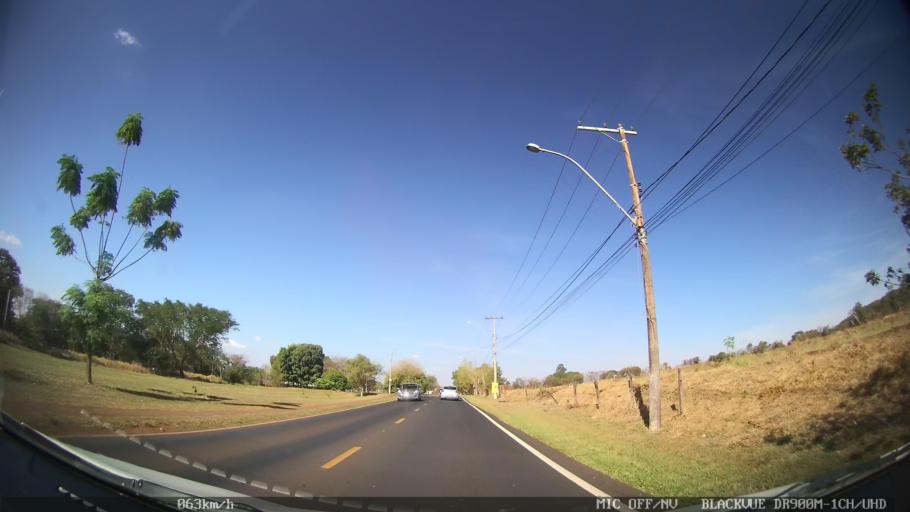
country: BR
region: Sao Paulo
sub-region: Ribeirao Preto
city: Ribeirao Preto
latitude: -21.1583
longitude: -47.7717
